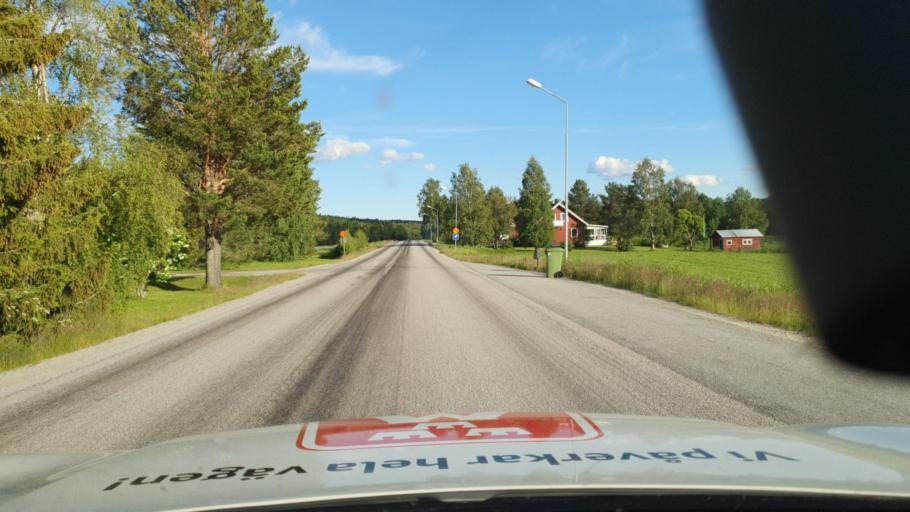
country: SE
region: Vaesterbotten
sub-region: Vindelns Kommun
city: Vindeln
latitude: 64.1611
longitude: 19.5011
